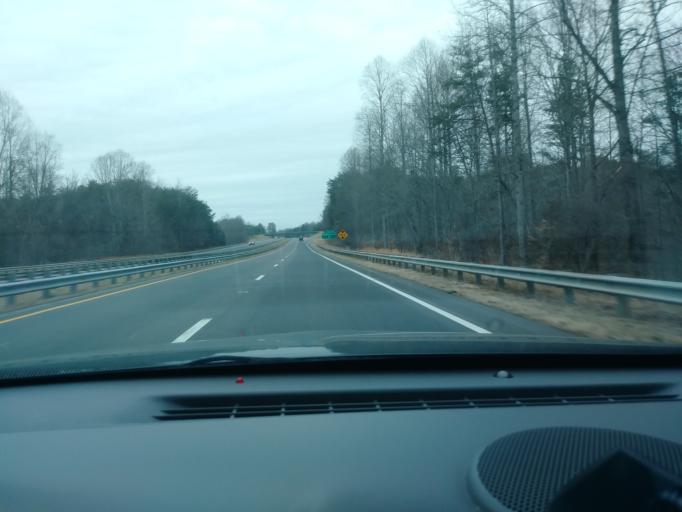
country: US
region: North Carolina
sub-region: Forsyth County
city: Lewisville
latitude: 36.0991
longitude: -80.4620
